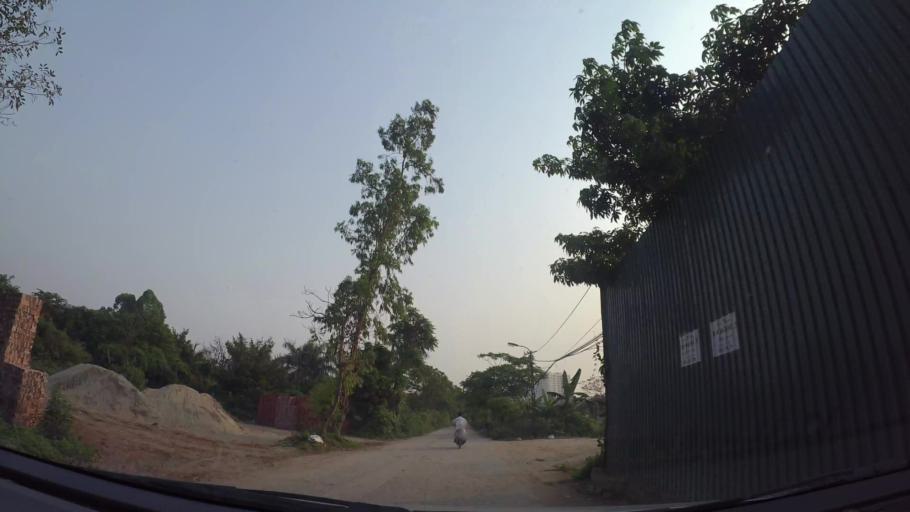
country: VN
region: Ha Noi
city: Tay Ho
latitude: 21.0746
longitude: 105.7951
